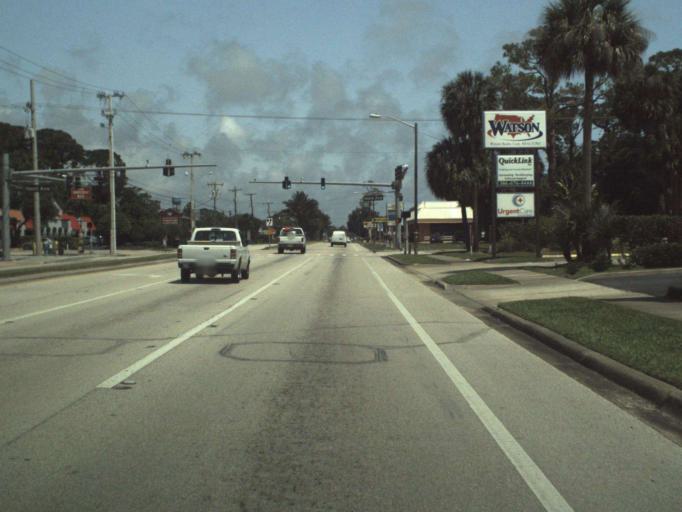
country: US
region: Florida
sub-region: Volusia County
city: Ormond Beach
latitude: 29.2713
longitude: -81.0558
